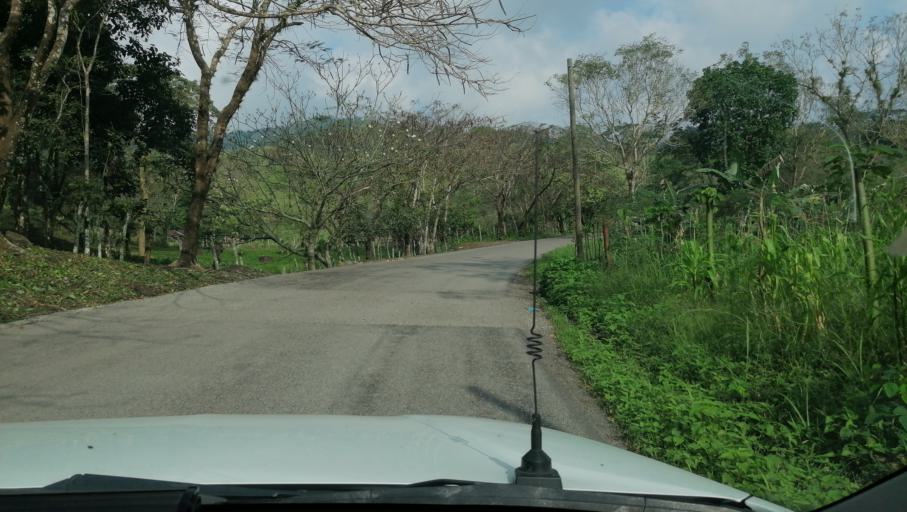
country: MX
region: Chiapas
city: Pichucalco
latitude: 17.5302
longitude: -93.1564
